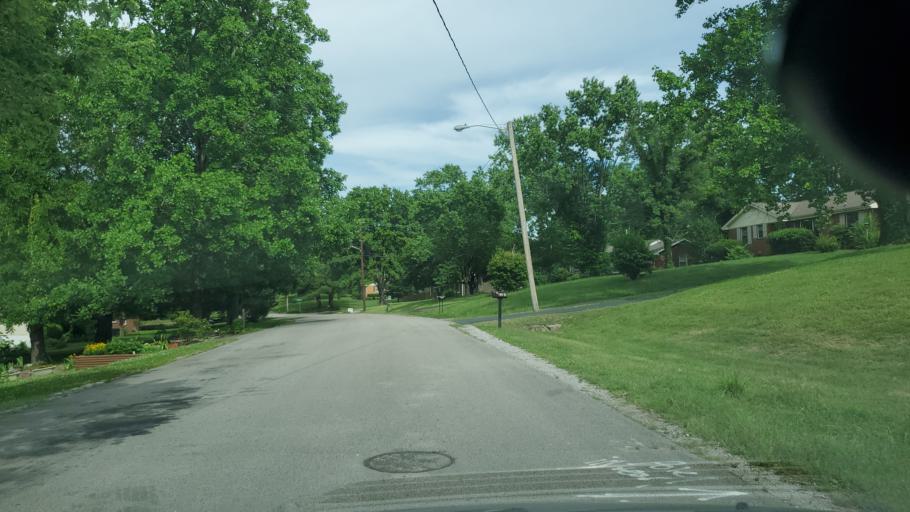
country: US
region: Tennessee
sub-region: Davidson County
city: Lakewood
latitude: 36.2012
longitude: -86.6826
